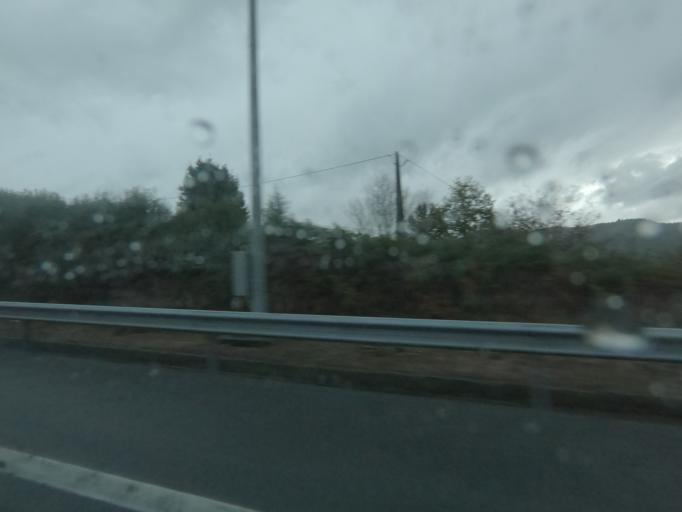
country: ES
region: Galicia
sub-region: Provincia de Pontevedra
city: Pontevedra
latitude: 42.3809
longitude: -8.6372
